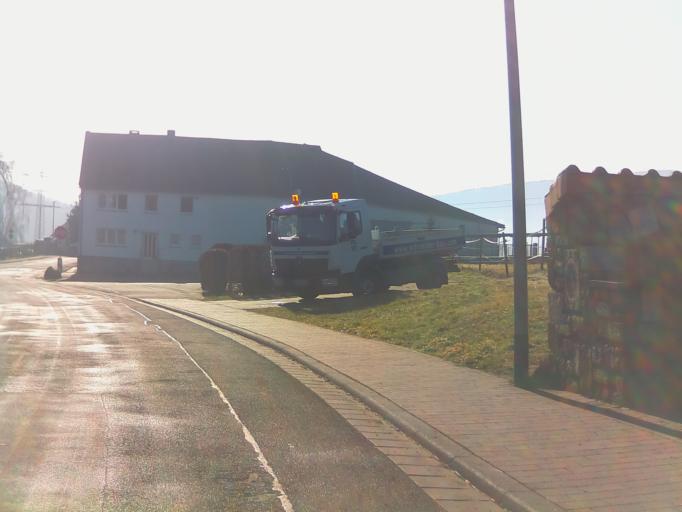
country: DE
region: Rheinland-Pfalz
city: Merxheim
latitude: 49.8076
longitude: 7.5589
